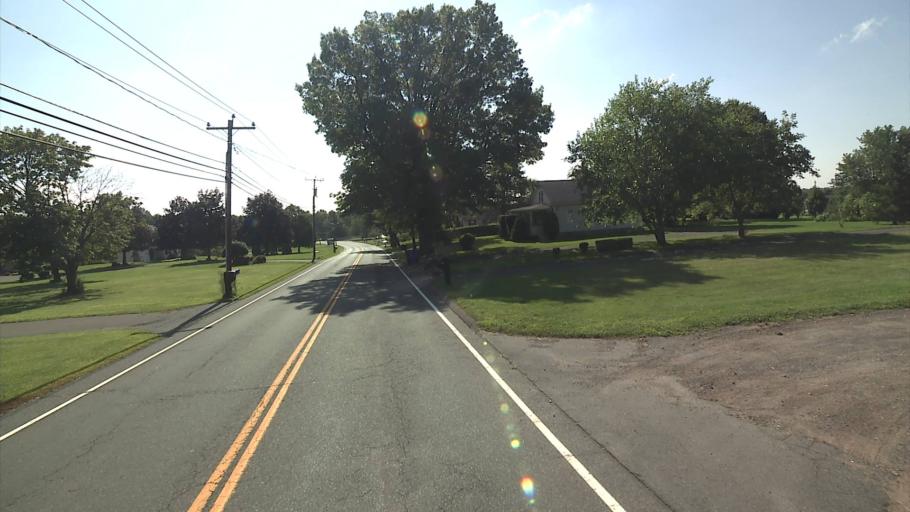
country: US
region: Connecticut
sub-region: Hartford County
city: Suffield Depot
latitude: 41.9983
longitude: -72.6317
